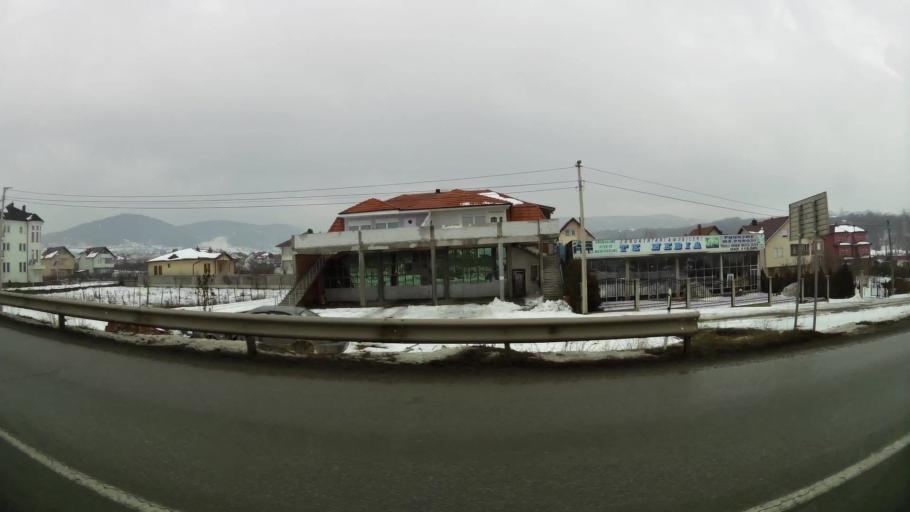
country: XK
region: Pristina
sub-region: Komuna e Prishtines
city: Pristina
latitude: 42.7093
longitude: 21.1532
